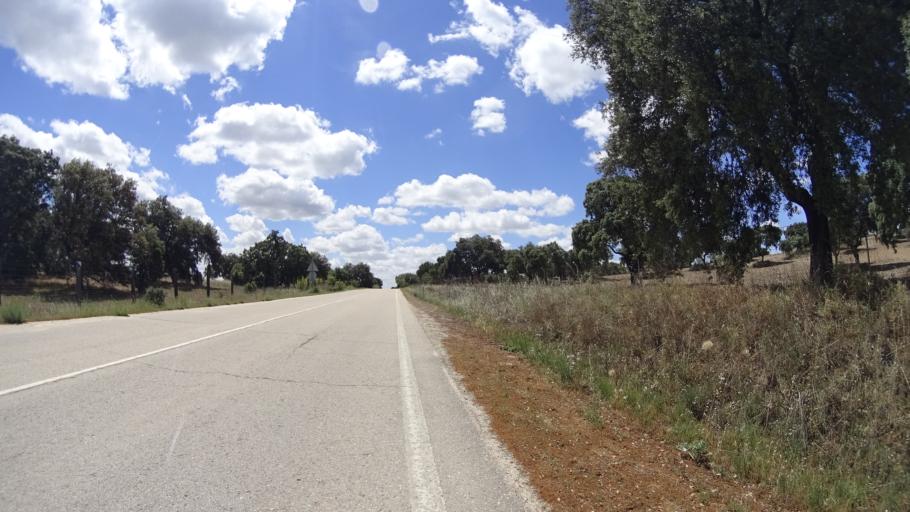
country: ES
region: Madrid
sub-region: Provincia de Madrid
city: Villanueva del Pardillo
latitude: 40.4501
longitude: -3.9533
